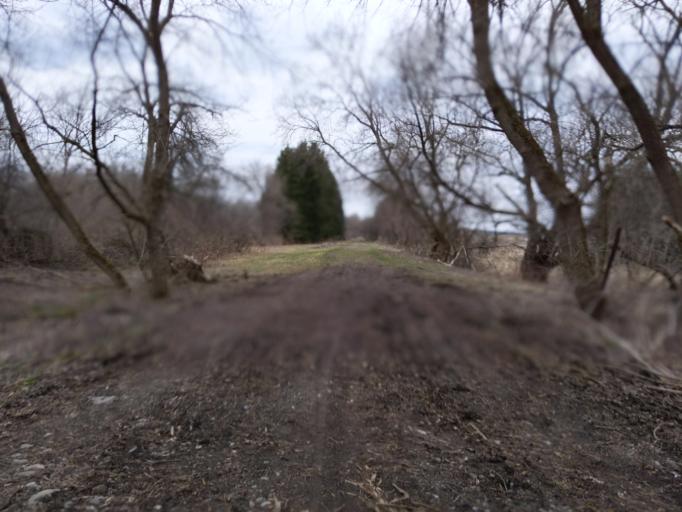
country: US
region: New York
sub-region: Tompkins County
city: Dryden
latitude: 42.5000
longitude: -76.3338
